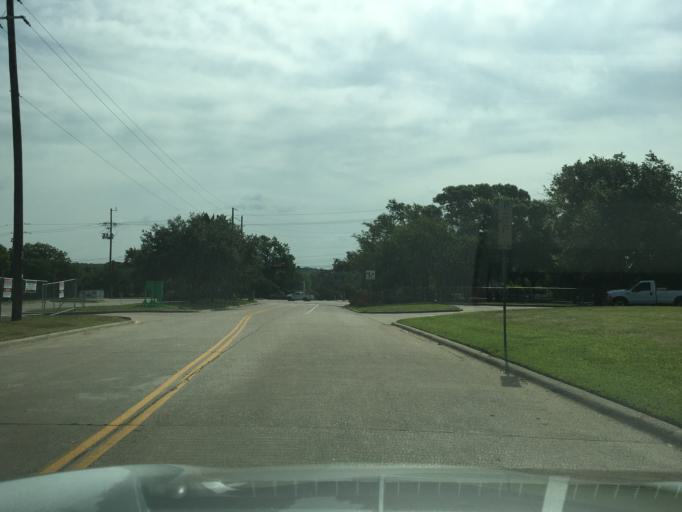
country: US
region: Texas
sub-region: Dallas County
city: Addison
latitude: 32.9237
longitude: -96.7904
